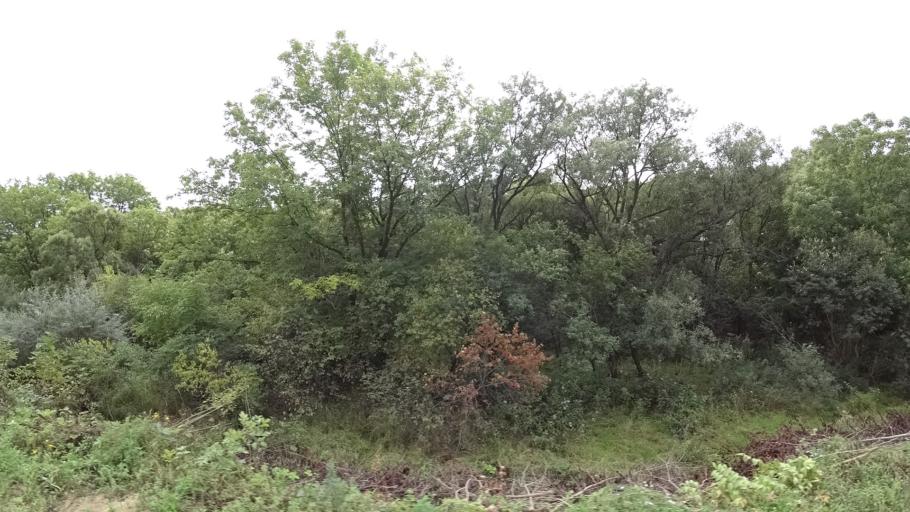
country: RU
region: Primorskiy
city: Lyalichi
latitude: 44.0824
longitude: 132.4476
